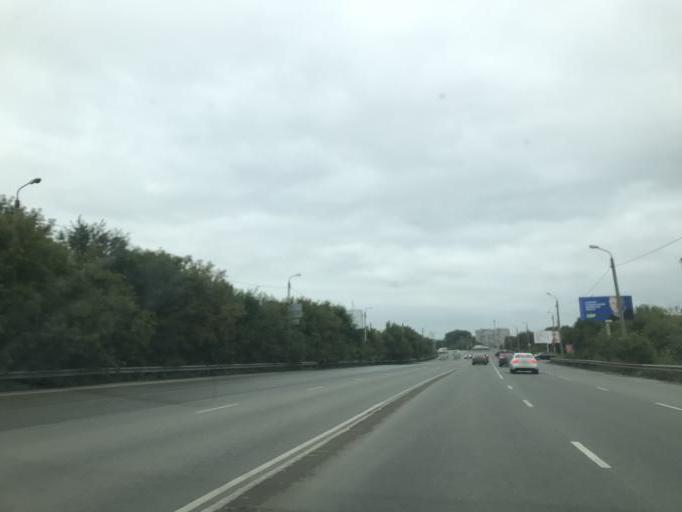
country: RU
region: Chelyabinsk
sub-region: Gorod Chelyabinsk
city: Chelyabinsk
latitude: 55.1648
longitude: 61.4281
